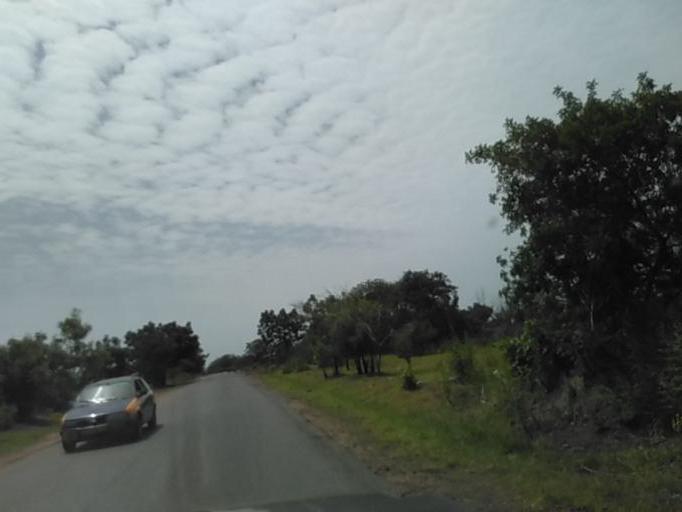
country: GH
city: Akropong
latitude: 6.0930
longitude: 0.0669
